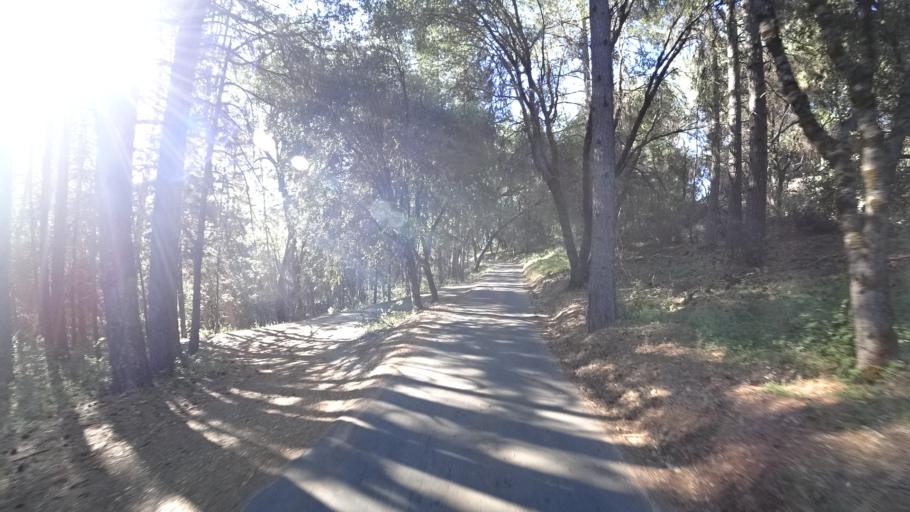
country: US
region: California
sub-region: Amador County
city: Pioneer
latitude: 38.3769
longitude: -120.5644
